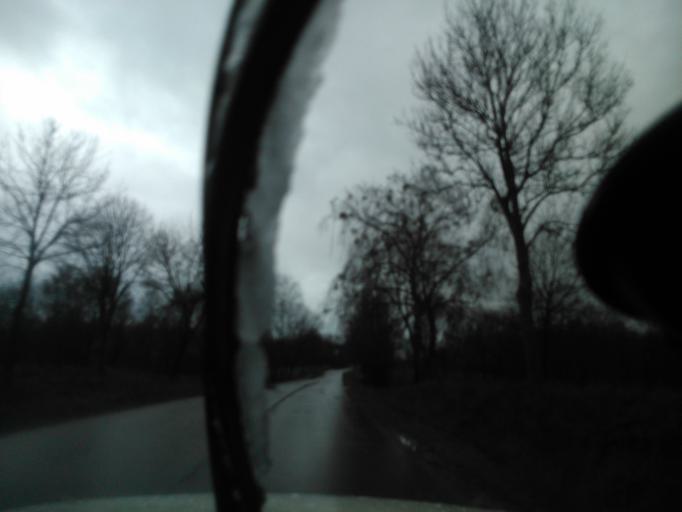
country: PL
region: Warmian-Masurian Voivodeship
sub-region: Powiat dzialdowski
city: Rybno
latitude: 53.3213
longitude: 19.8939
